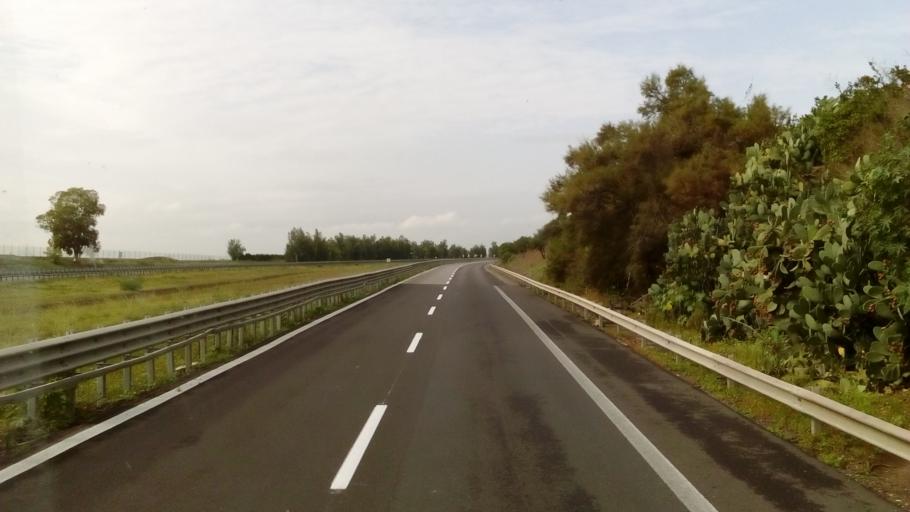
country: IT
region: Sicily
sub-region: Catania
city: Motta Sant'Anastasia
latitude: 37.4681
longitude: 14.8742
